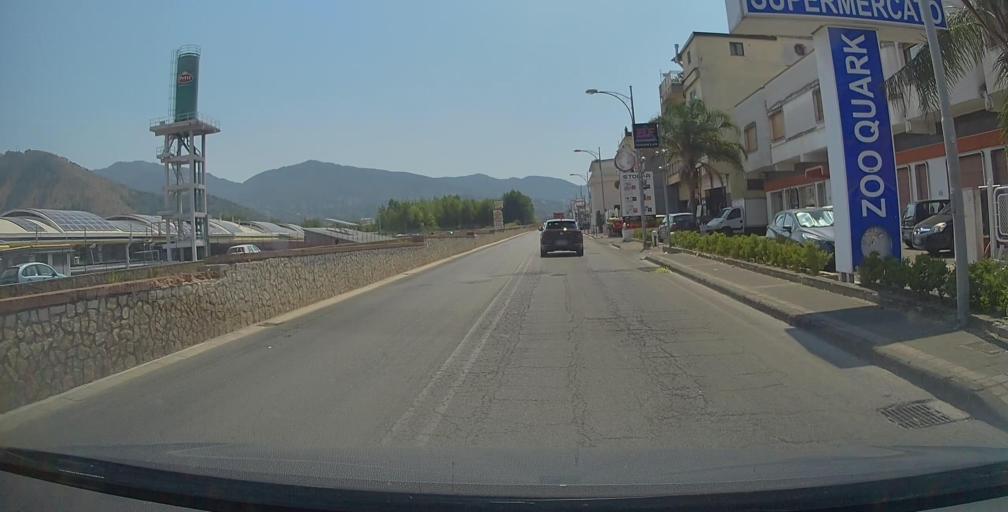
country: IT
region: Campania
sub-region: Provincia di Salerno
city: Nocera Superiore
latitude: 40.7388
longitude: 14.6734
